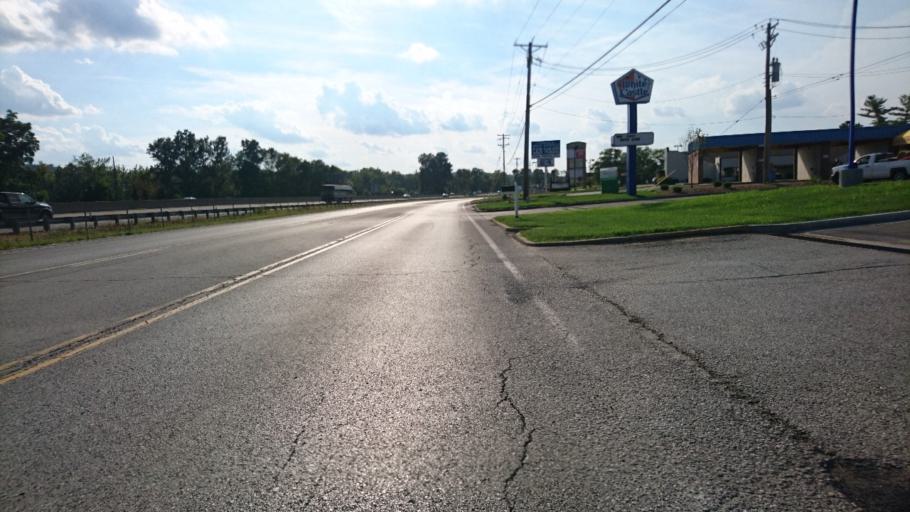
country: US
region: Missouri
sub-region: Saint Louis County
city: Eureka
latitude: 38.5047
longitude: -90.6406
